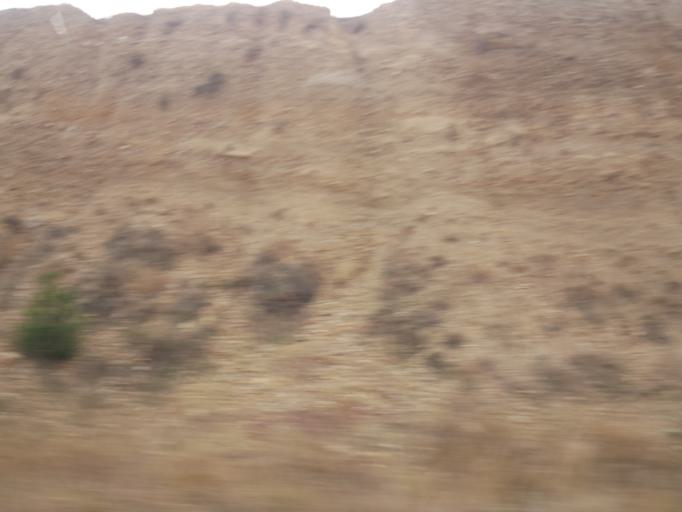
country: TR
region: Sinop
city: Sarayduzu
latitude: 41.3450
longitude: 34.8292
